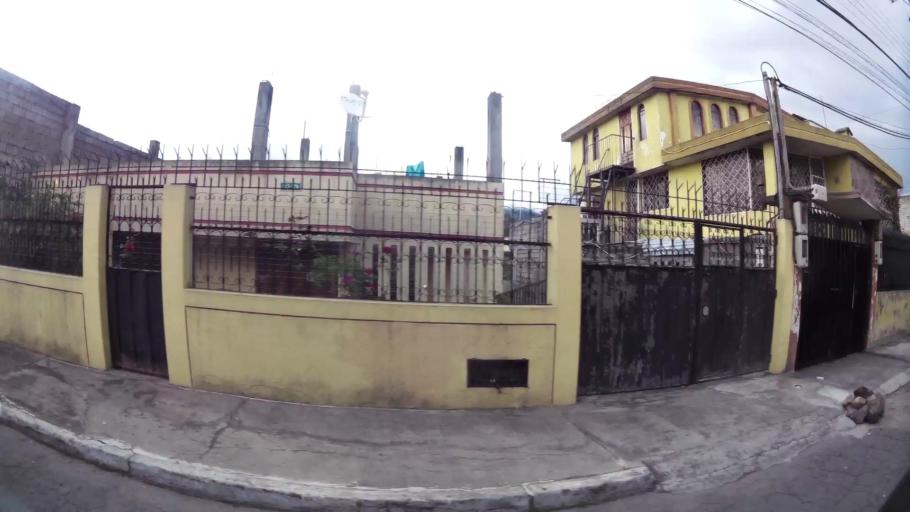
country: EC
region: Pichincha
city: Quito
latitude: -0.2836
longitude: -78.5399
